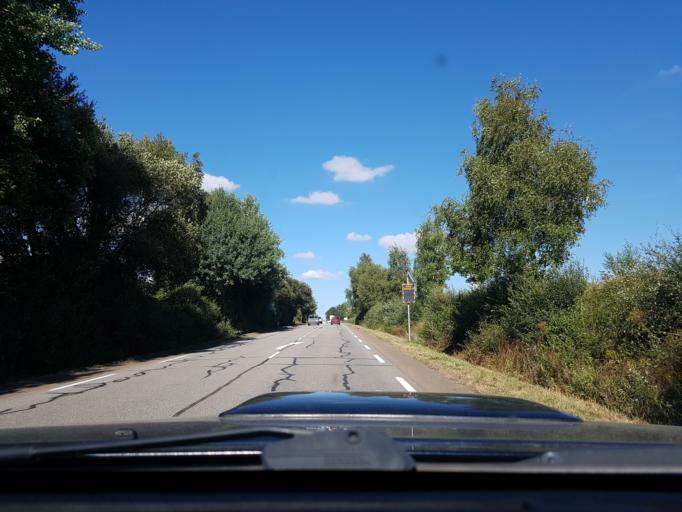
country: FR
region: Pays de la Loire
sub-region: Departement de la Vendee
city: Aizenay
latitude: 46.7325
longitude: -1.6258
